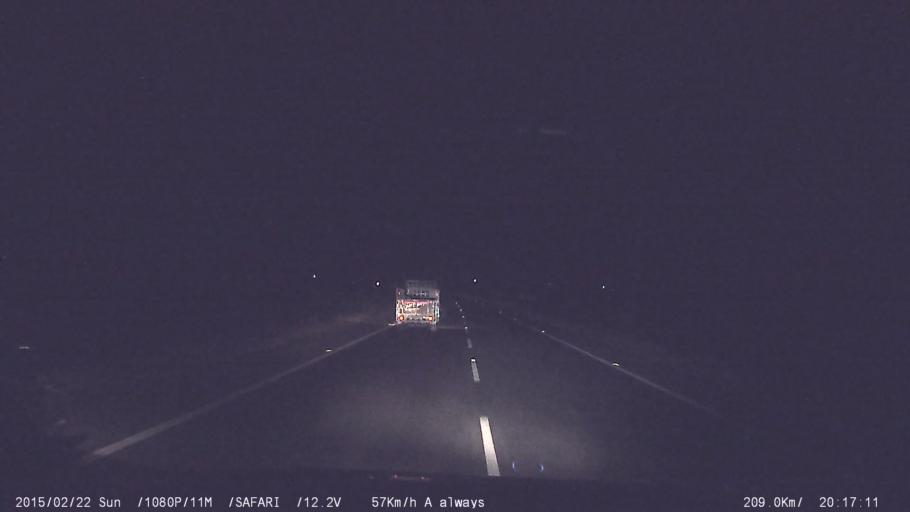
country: IN
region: Tamil Nadu
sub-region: Dindigul
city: Nilakottai
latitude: 10.2670
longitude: 77.8578
